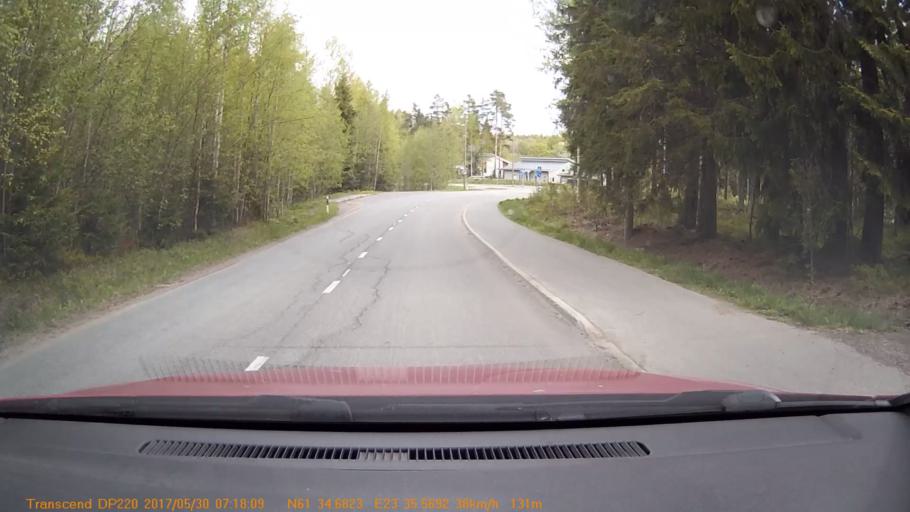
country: FI
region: Pirkanmaa
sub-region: Tampere
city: Yloejaervi
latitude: 61.5779
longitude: 23.5928
